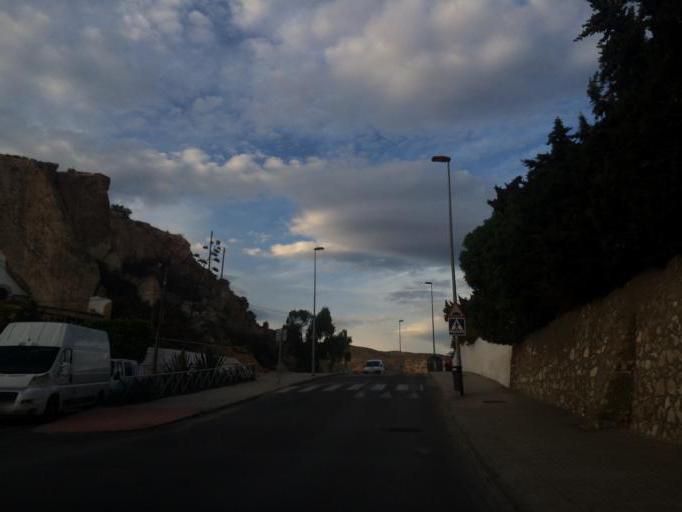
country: ES
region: Andalusia
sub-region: Provincia de Almeria
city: Almeria
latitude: 36.8499
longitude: -2.4702
